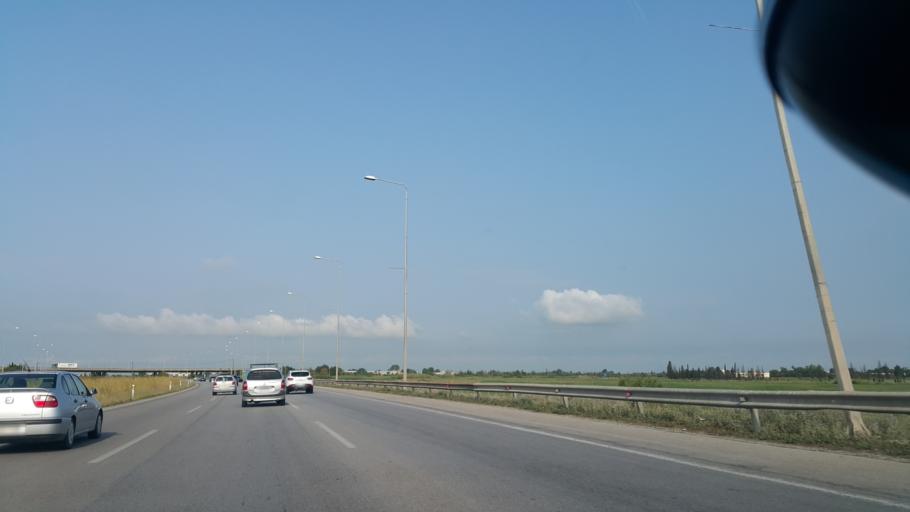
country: GR
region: Central Macedonia
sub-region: Nomos Thessalonikis
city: Sindos
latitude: 40.6513
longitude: 22.8185
